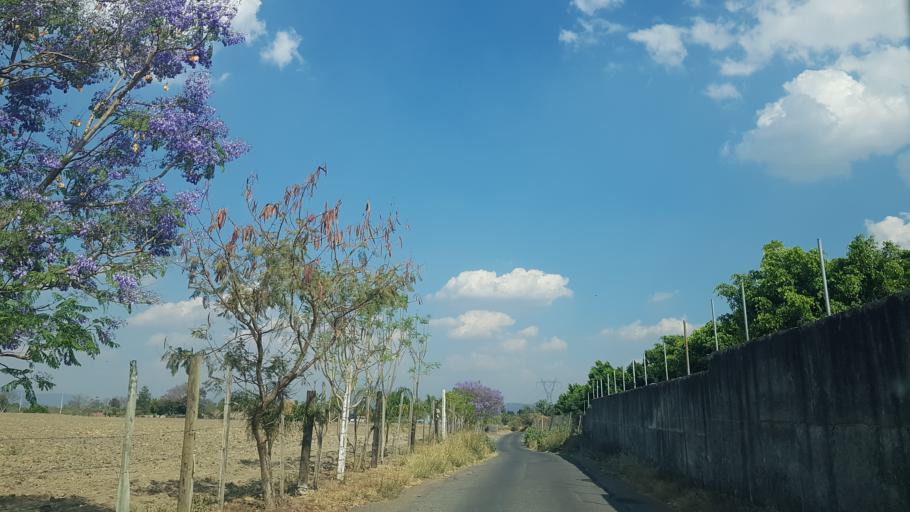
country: MX
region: Puebla
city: Atlixco
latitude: 18.8813
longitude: -98.4885
